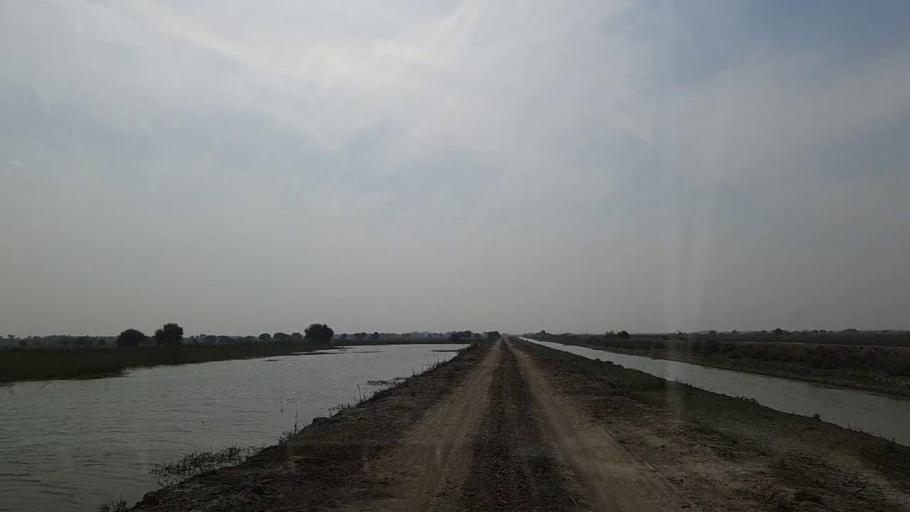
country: PK
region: Sindh
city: Mirpur Batoro
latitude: 24.6728
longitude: 68.2496
